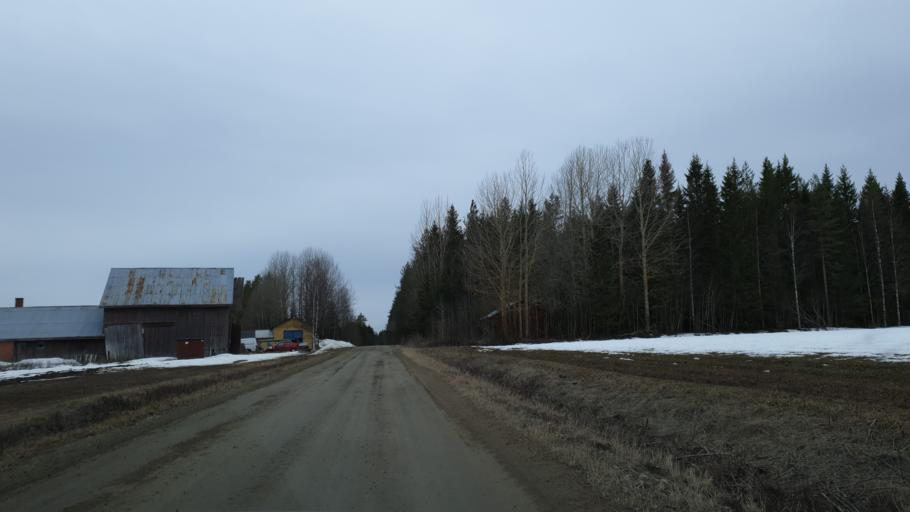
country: SE
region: Vaesterbotten
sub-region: Robertsfors Kommun
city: Robertsfors
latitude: 64.3876
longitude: 20.9455
